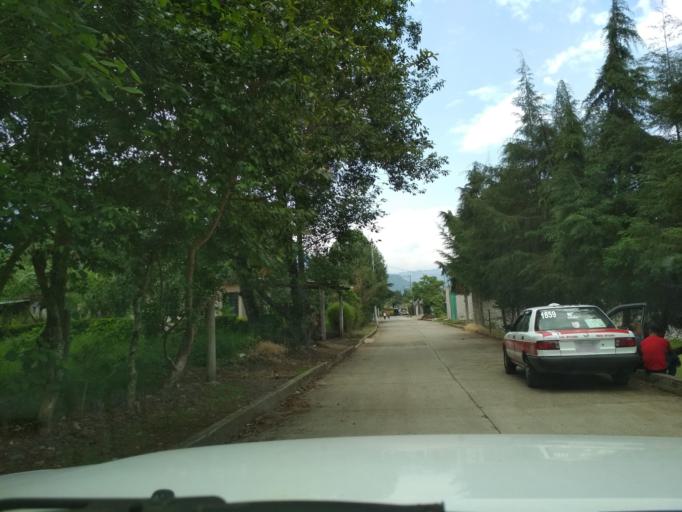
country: MX
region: Veracruz
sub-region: Mariano Escobedo
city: Mariano Escobedo
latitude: 18.9131
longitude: -97.1261
